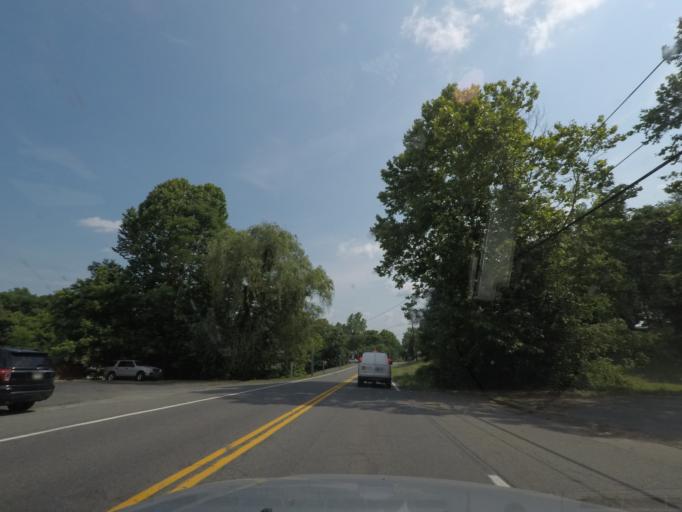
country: US
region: Virginia
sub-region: Fluvanna County
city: Palmyra
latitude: 37.8620
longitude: -78.2636
